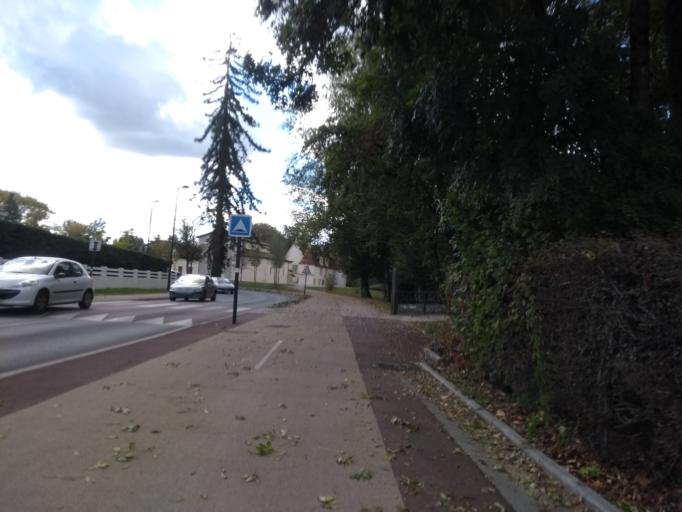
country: FR
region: Aquitaine
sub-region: Departement de la Gironde
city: Gradignan
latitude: 44.7660
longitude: -0.6178
